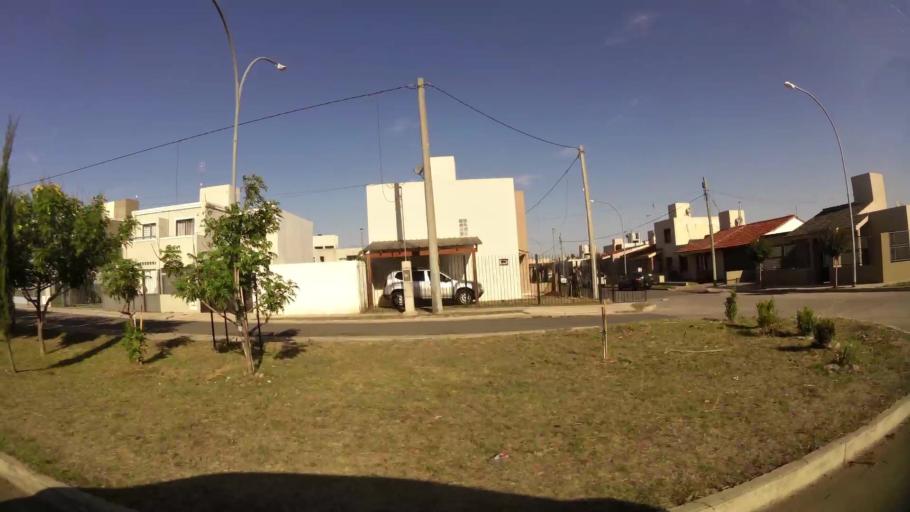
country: AR
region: Cordoba
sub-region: Departamento de Capital
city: Cordoba
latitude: -31.3559
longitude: -64.2254
